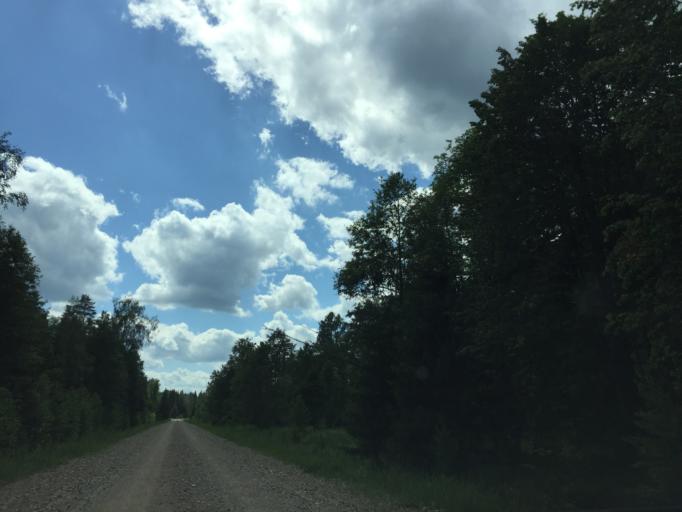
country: LV
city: Tireli
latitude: 56.8406
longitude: 23.6985
